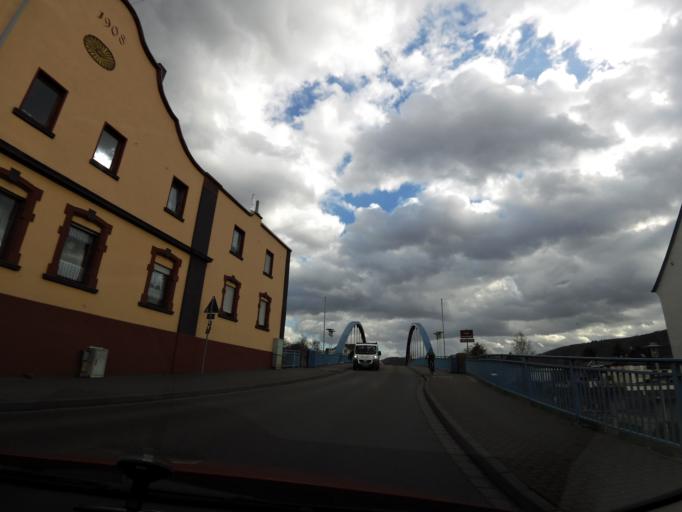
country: DE
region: Rheinland-Pfalz
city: Lahnstein
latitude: 50.3090
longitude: 7.6040
